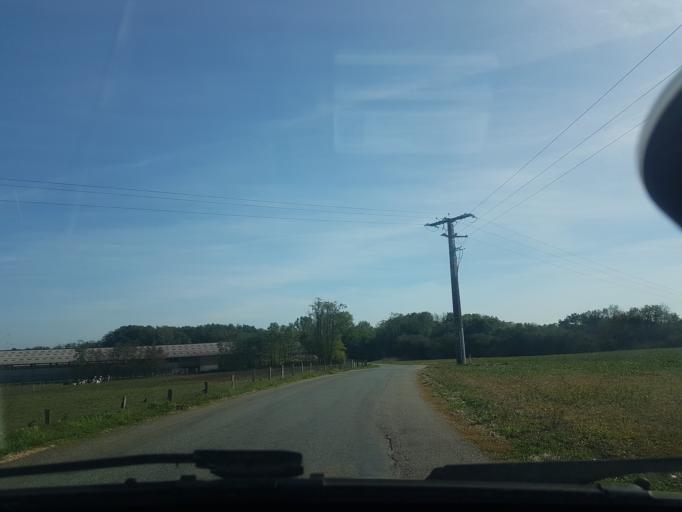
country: FR
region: Franche-Comte
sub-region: Territoire de Belfort
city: Chevremont
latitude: 47.6547
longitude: 6.9214
